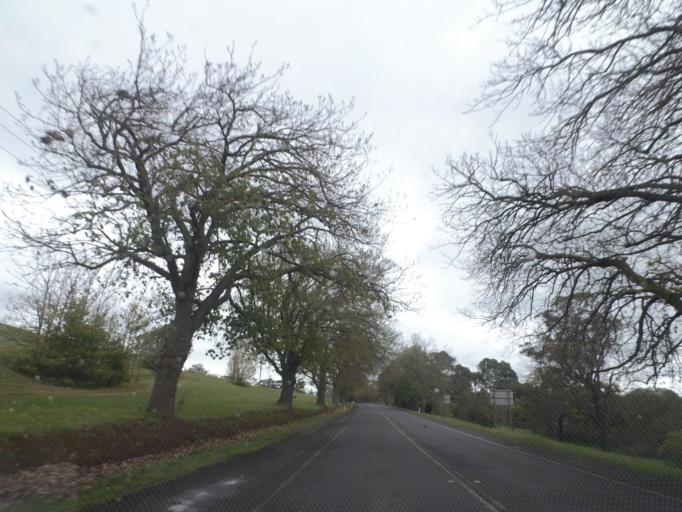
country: AU
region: Victoria
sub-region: Hume
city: Sunbury
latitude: -37.3435
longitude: 144.5320
